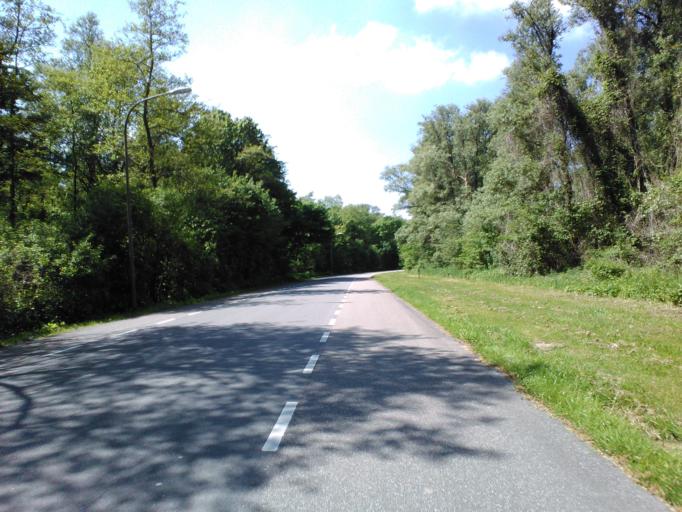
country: NL
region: South Holland
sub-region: Gemeente Sliedrecht
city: Sliedrecht
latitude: 51.8096
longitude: 4.7564
